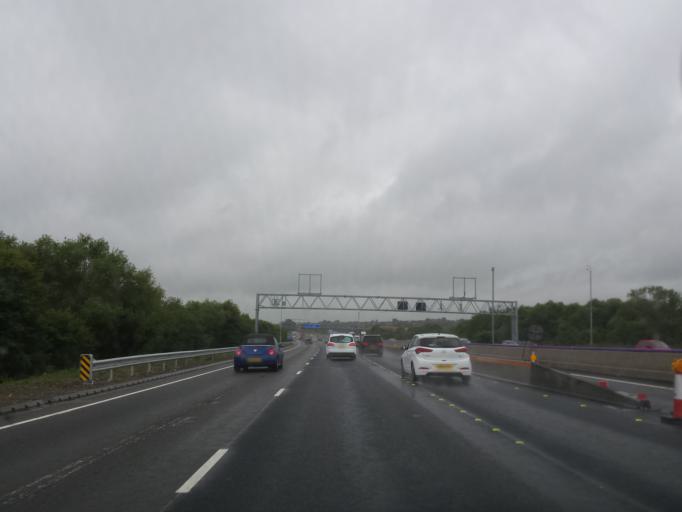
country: GB
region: England
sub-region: Derbyshire
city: Staveley
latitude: 53.2549
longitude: -1.3229
